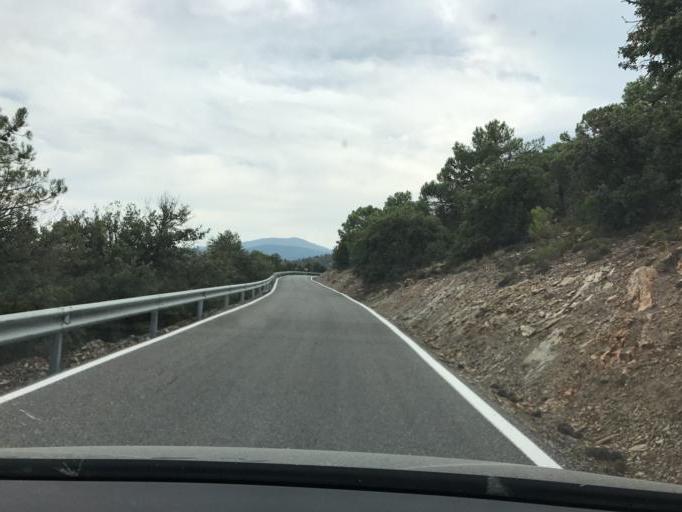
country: ES
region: Andalusia
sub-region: Provincia de Granada
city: Aldeire
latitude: 37.1558
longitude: -3.0504
